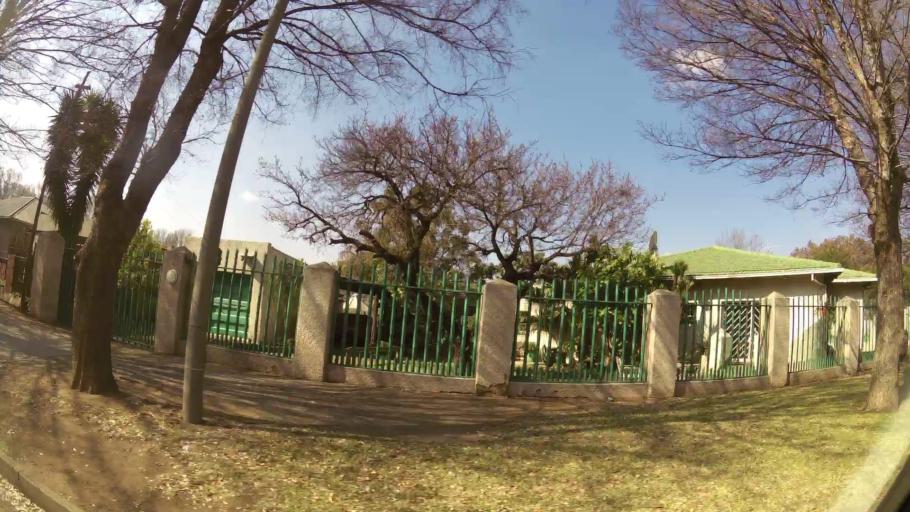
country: ZA
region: Gauteng
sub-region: Ekurhuleni Metropolitan Municipality
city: Boksburg
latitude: -26.2044
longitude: 28.2376
